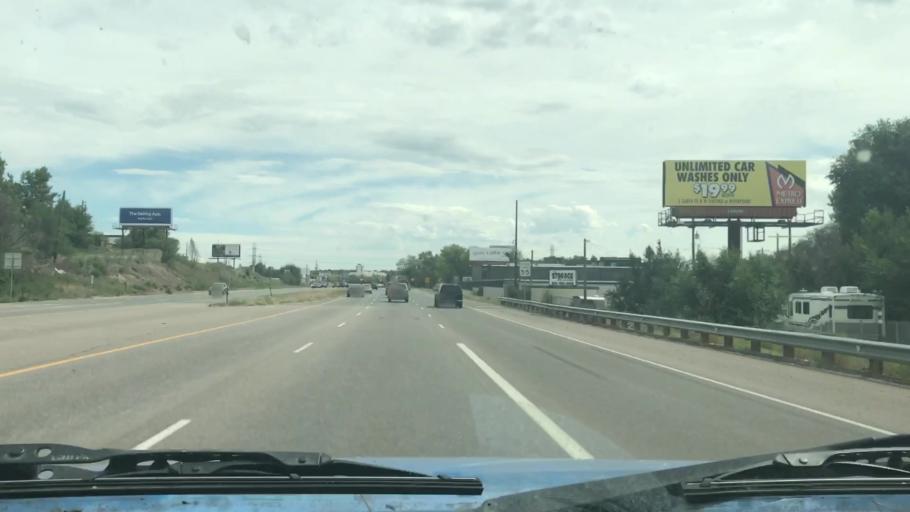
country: US
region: Colorado
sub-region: Arapahoe County
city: Sheridan
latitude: 39.6522
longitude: -105.0227
